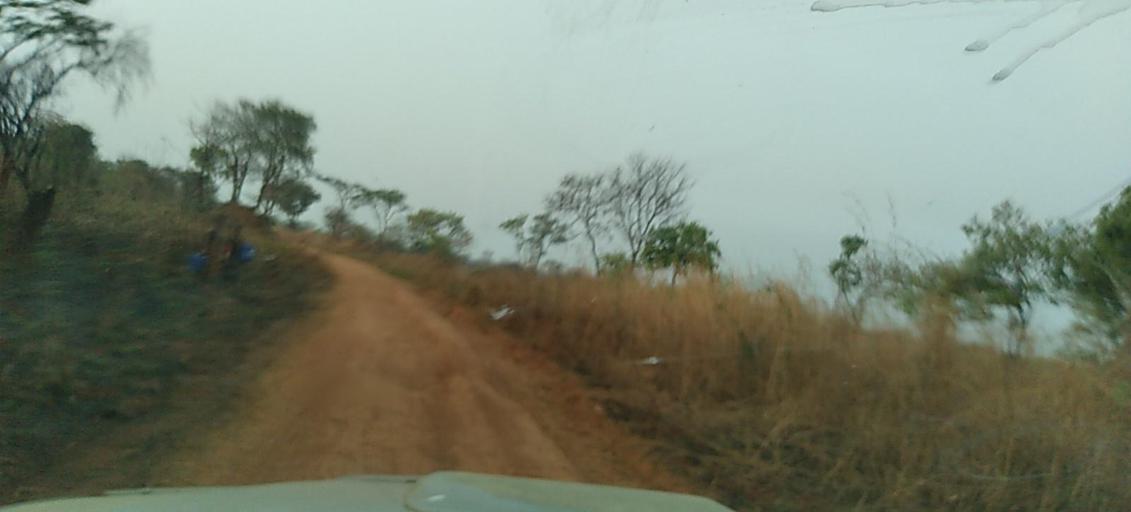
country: ZM
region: North-Western
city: Kasempa
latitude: -13.0664
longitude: 26.3815
